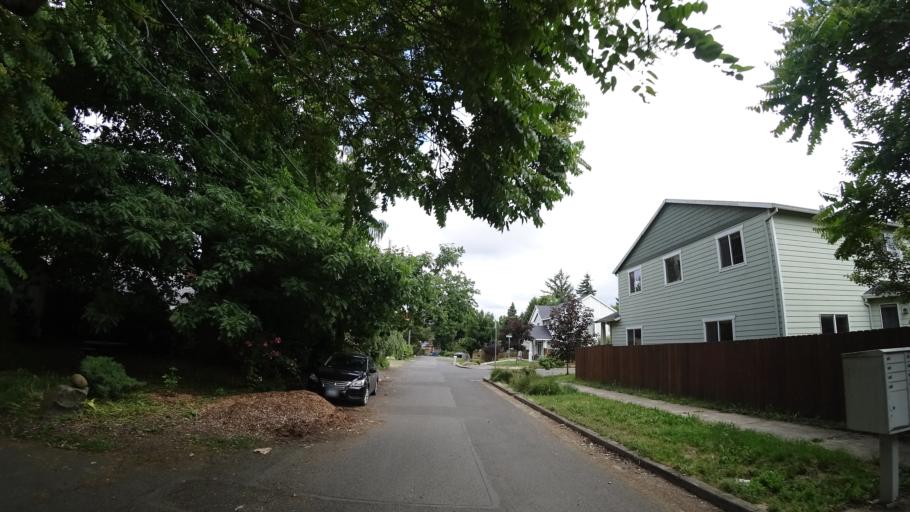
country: US
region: Oregon
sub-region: Multnomah County
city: Portland
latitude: 45.5634
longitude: -122.6134
